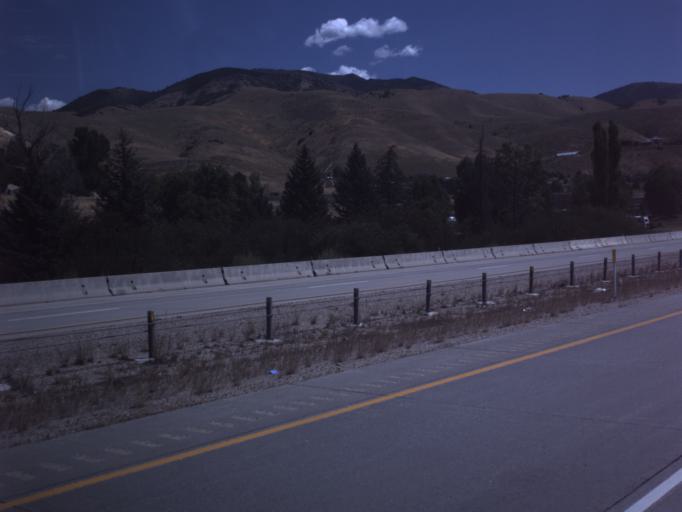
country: US
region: Utah
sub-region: Morgan County
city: Mountain Green
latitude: 41.1119
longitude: -111.7583
